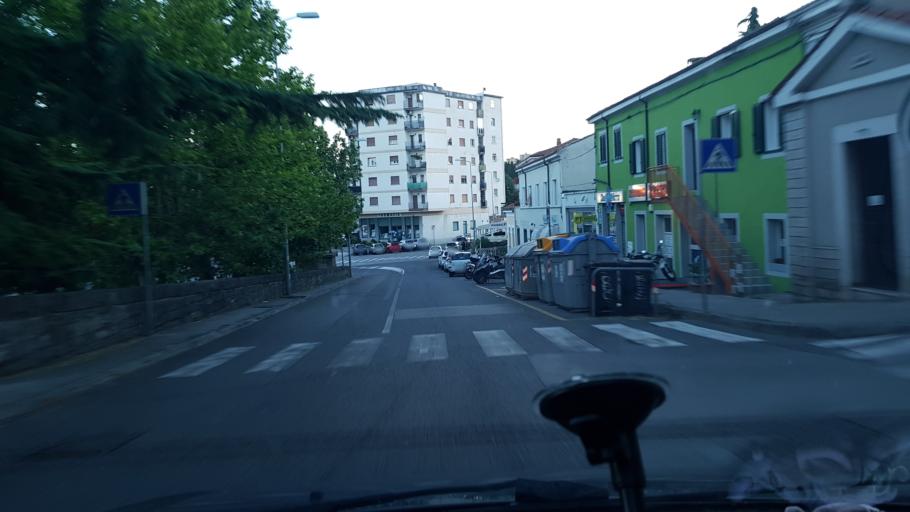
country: IT
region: Friuli Venezia Giulia
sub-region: Provincia di Trieste
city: Trieste
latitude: 45.6251
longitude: 13.7957
